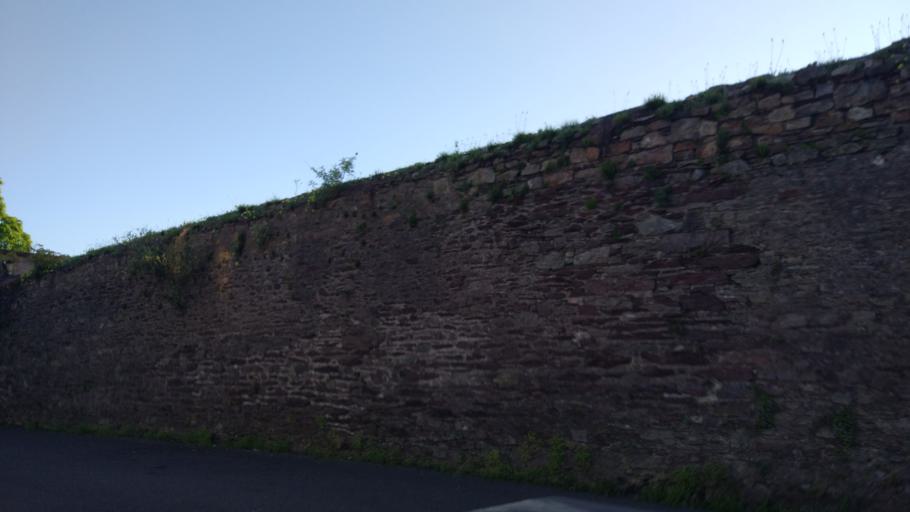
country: IE
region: Munster
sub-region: County Cork
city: Cork
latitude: 51.9080
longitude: -8.4606
